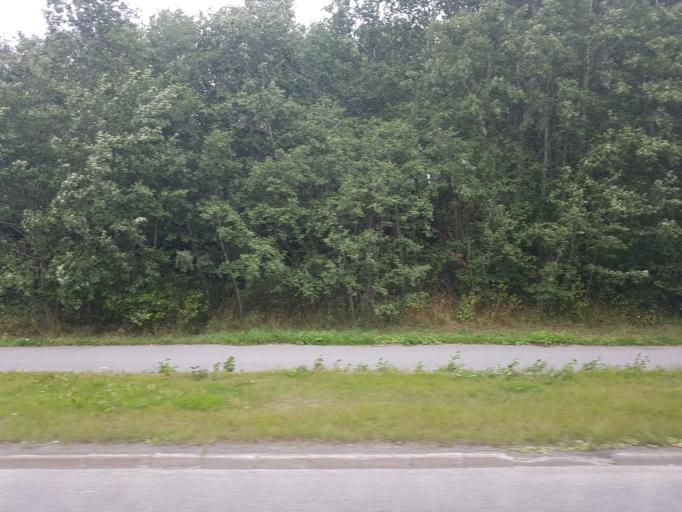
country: NO
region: Sor-Trondelag
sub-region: Trondheim
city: Trondheim
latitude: 63.3947
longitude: 10.4027
